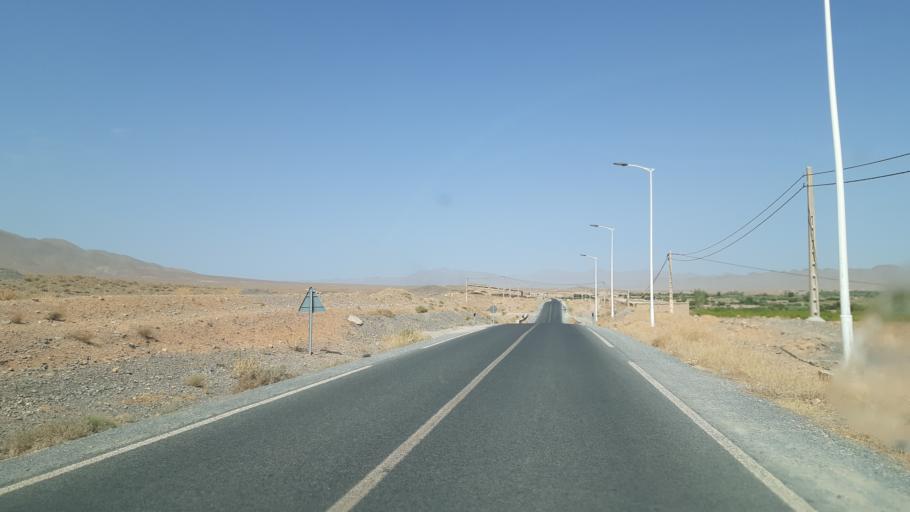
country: MA
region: Meknes-Tafilalet
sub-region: Errachidia
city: Amouguer
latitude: 32.2225
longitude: -4.6829
